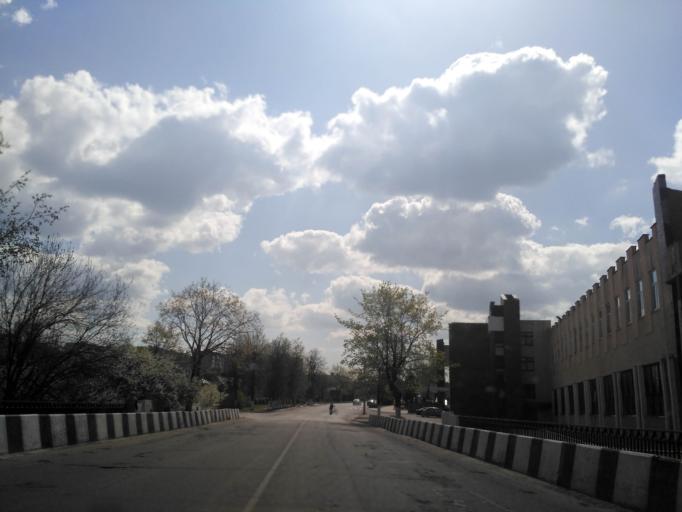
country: BY
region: Minsk
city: Radashkovichy
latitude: 54.1574
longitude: 27.2405
